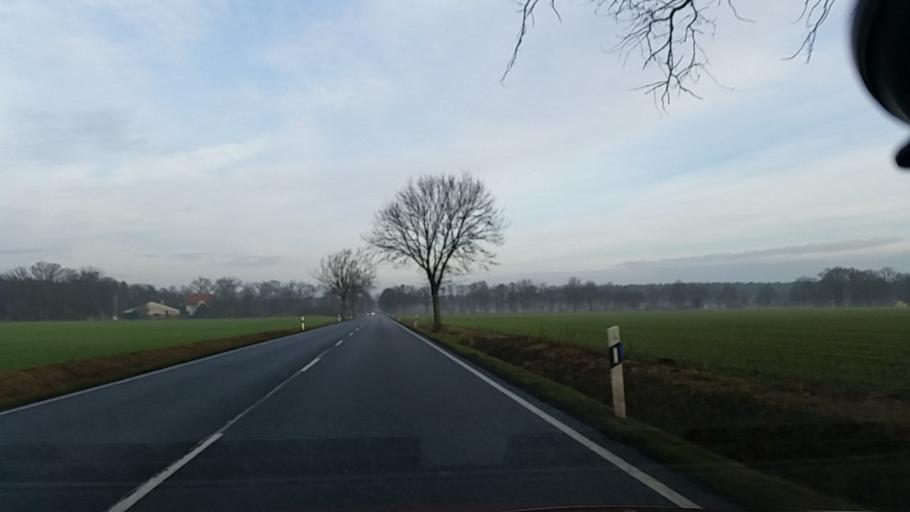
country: DE
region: Lower Saxony
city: Barwedel
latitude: 52.5321
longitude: 10.7792
